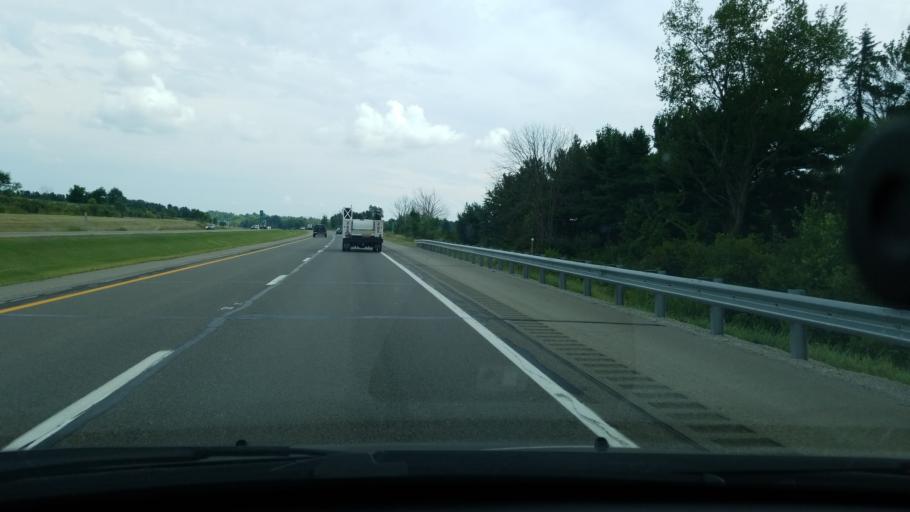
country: US
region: Ohio
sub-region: Mahoning County
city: Boardman
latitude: 40.9851
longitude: -80.6855
